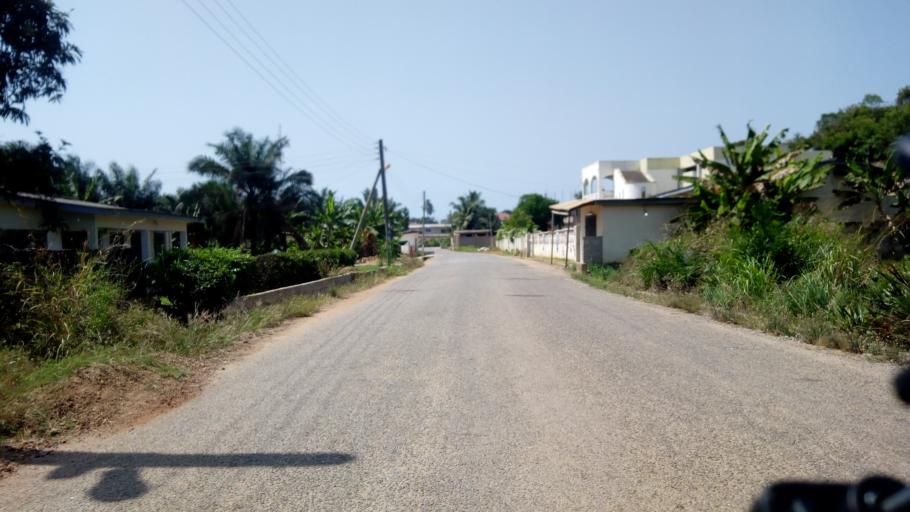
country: GH
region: Central
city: Cape Coast
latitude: 5.1103
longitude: -1.2713
